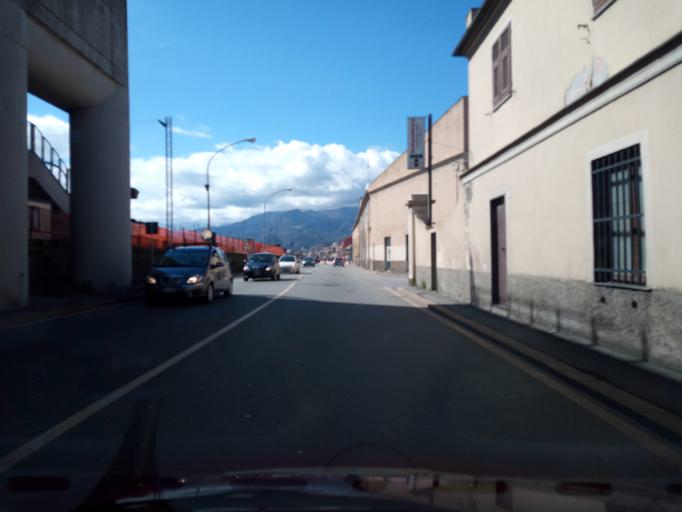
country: IT
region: Liguria
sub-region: Provincia di Genova
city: Mele
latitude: 44.4254
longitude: 8.7964
